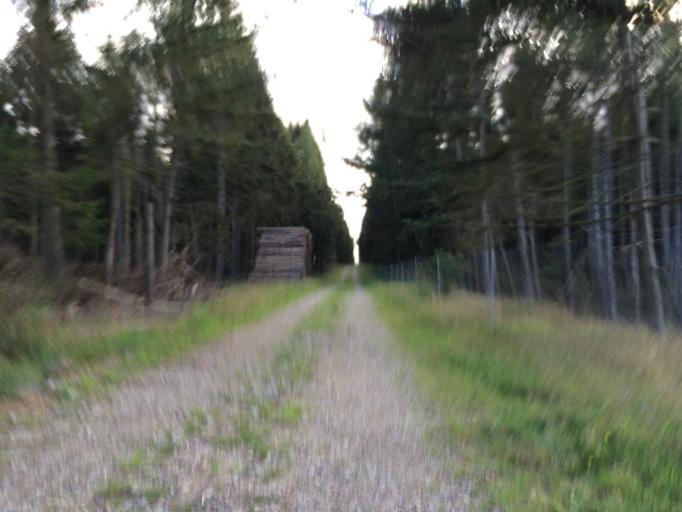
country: DK
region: Central Jutland
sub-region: Holstebro Kommune
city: Ulfborg
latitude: 56.2688
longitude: 8.4414
